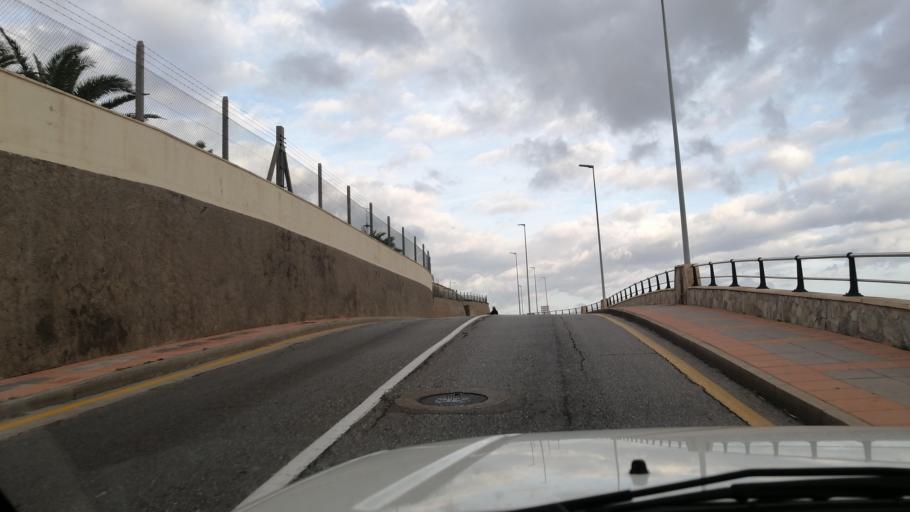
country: ES
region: Ceuta
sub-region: Ceuta
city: Ceuta
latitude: 35.8855
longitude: -5.3066
